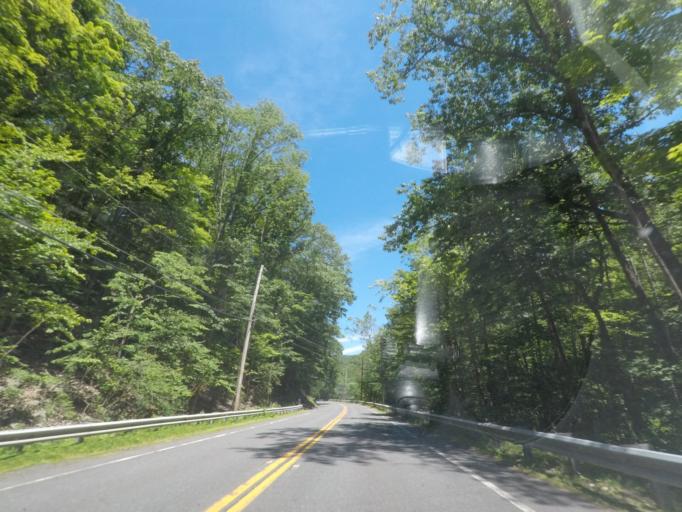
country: US
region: Massachusetts
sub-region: Berkshire County
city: Becket
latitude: 42.2778
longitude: -72.9914
